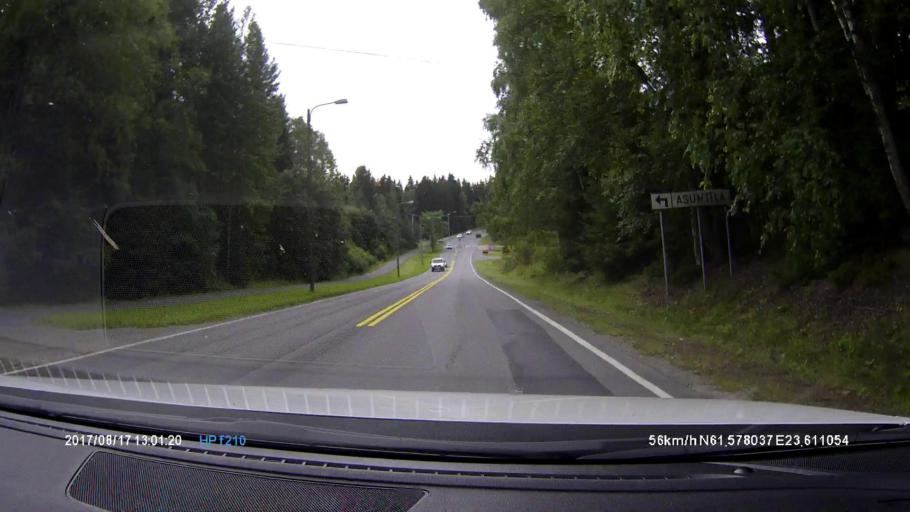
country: FI
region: Pirkanmaa
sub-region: Tampere
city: Yloejaervi
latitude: 61.5774
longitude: 23.6108
